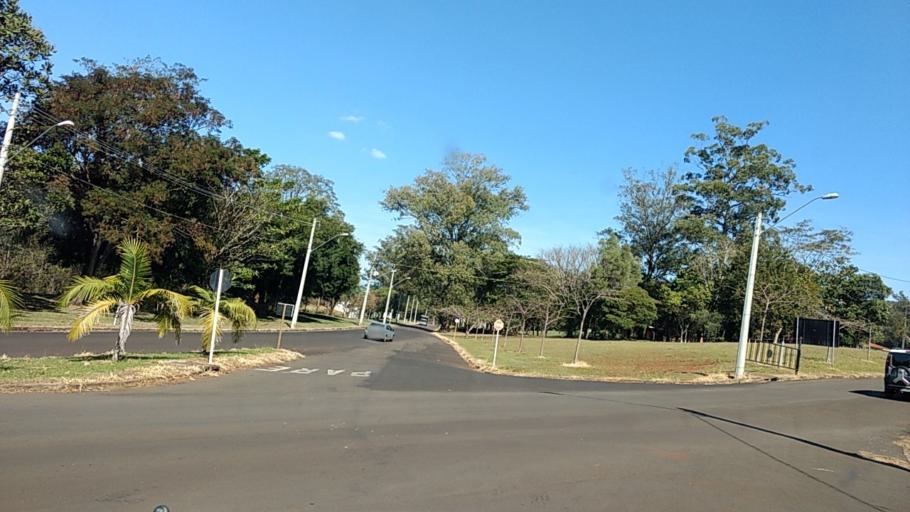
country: BR
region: Sao Paulo
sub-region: Botucatu
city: Botucatu
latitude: -22.8503
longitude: -48.4318
